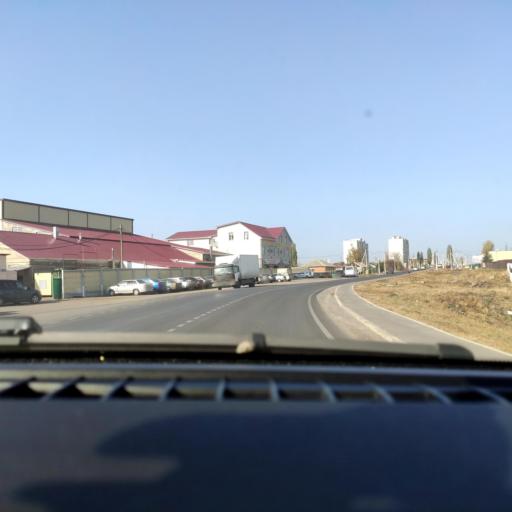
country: RU
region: Voronezj
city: Novaya Usman'
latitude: 51.6500
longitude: 39.4132
